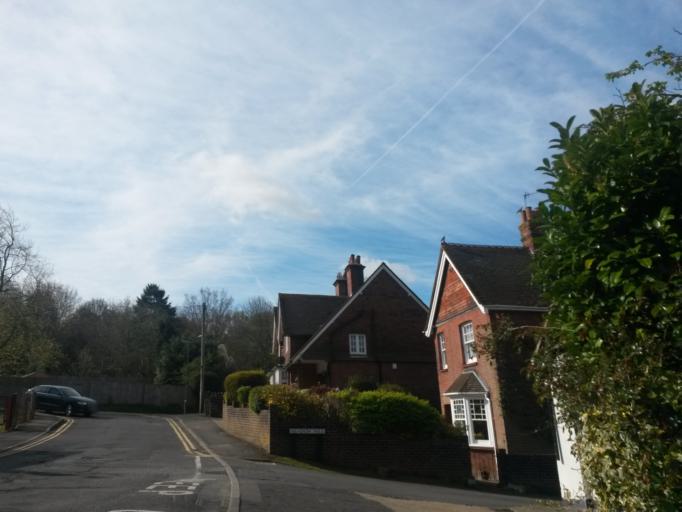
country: GB
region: England
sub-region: Surrey
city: Haslemere
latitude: 51.0872
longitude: -0.7284
